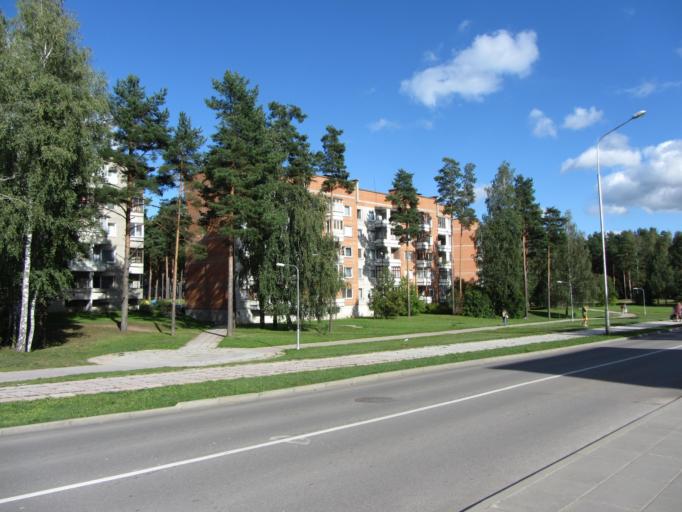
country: LT
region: Utenos apskritis
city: Visaginas
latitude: 55.5959
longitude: 26.4432
